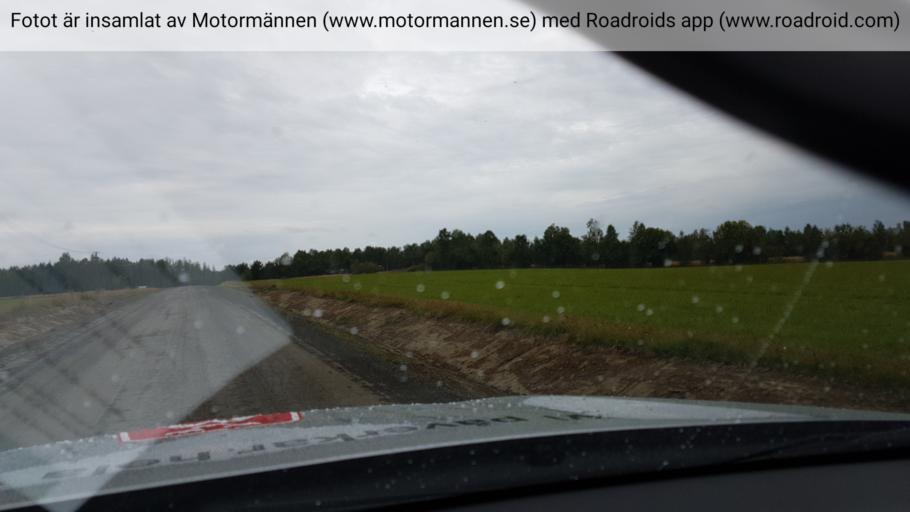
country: SE
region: Norrbotten
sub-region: Alvsbyns Kommun
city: AElvsbyn
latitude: 65.9080
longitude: 21.2947
